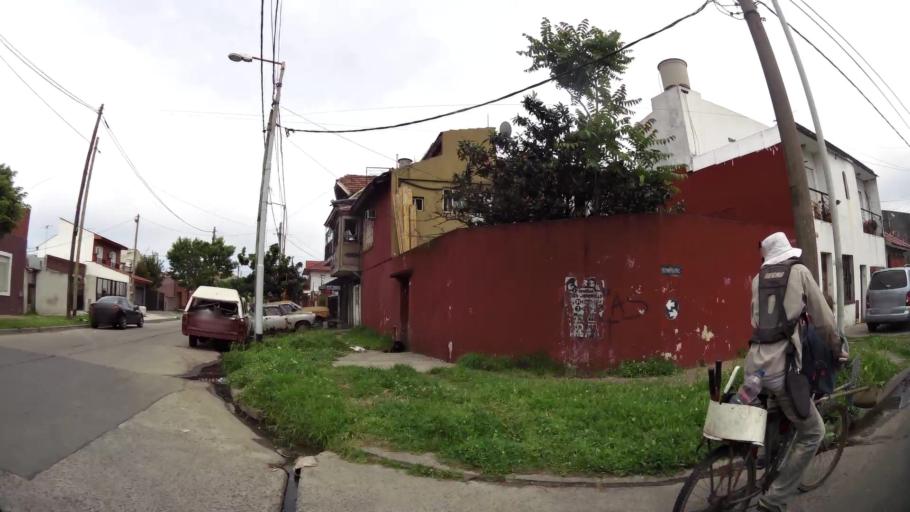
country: AR
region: Buenos Aires
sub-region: Partido de Avellaneda
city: Avellaneda
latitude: -34.6658
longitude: -58.3455
